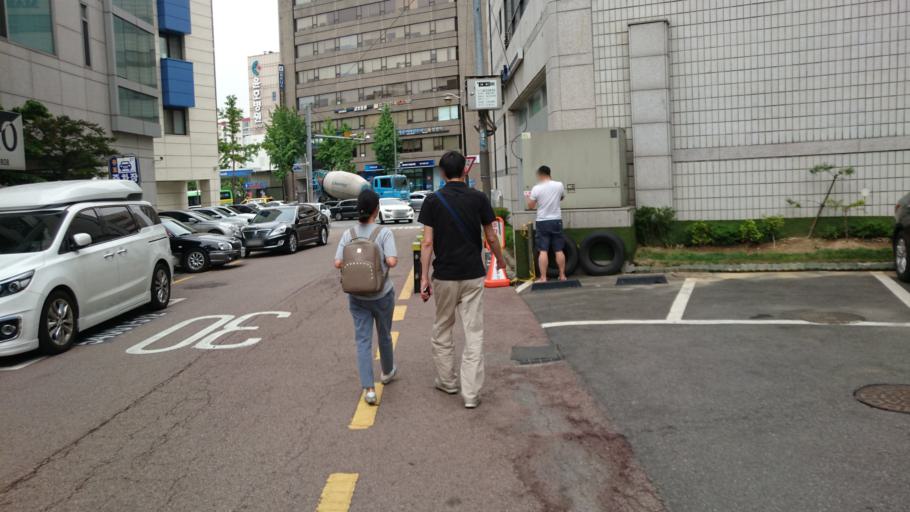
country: KR
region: Seoul
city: Seoul
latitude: 37.5283
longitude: 127.0330
